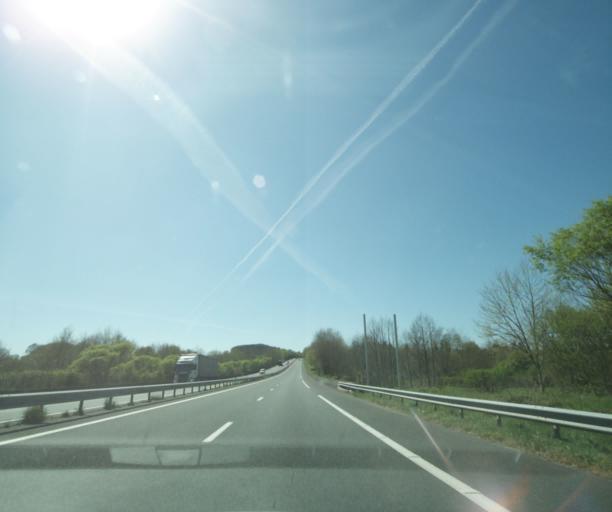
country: FR
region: Limousin
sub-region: Departement de la Haute-Vienne
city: Saint-Sulpice-les-Feuilles
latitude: 46.3805
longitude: 1.4475
